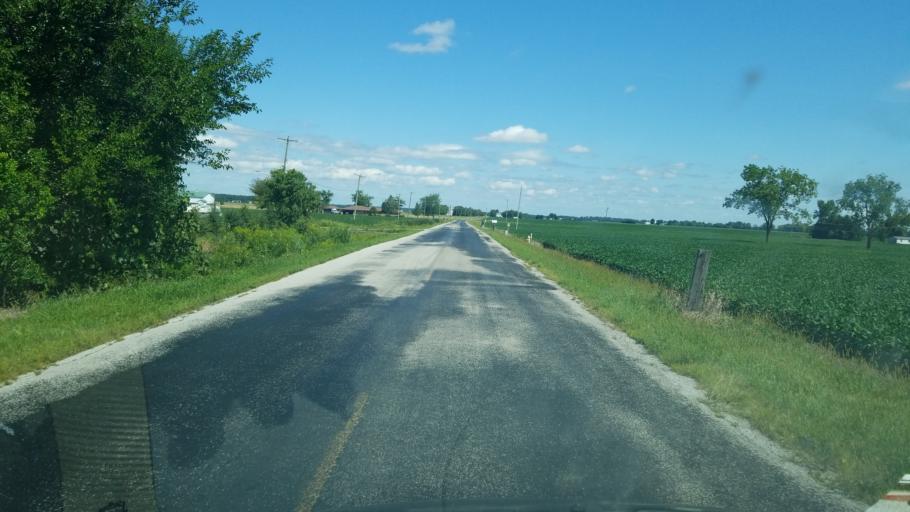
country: US
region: Ohio
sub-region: Wood County
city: Weston
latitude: 41.2955
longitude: -83.8440
